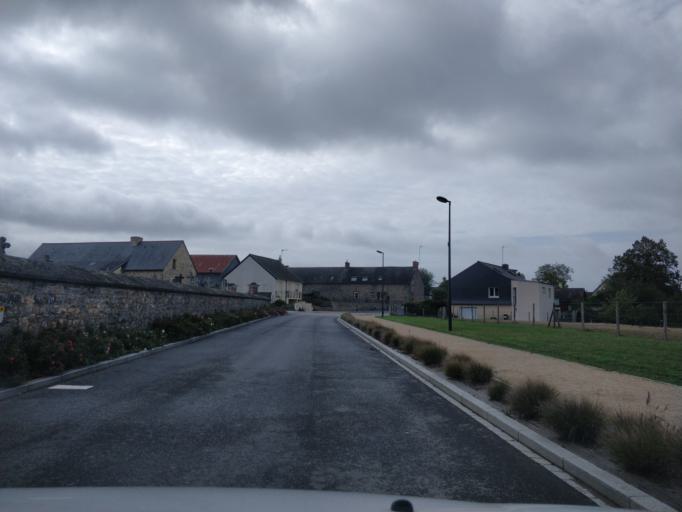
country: FR
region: Brittany
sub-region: Departement d'Ille-et-Vilaine
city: Servon-sur-Vilaine
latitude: 48.1245
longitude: -1.4586
